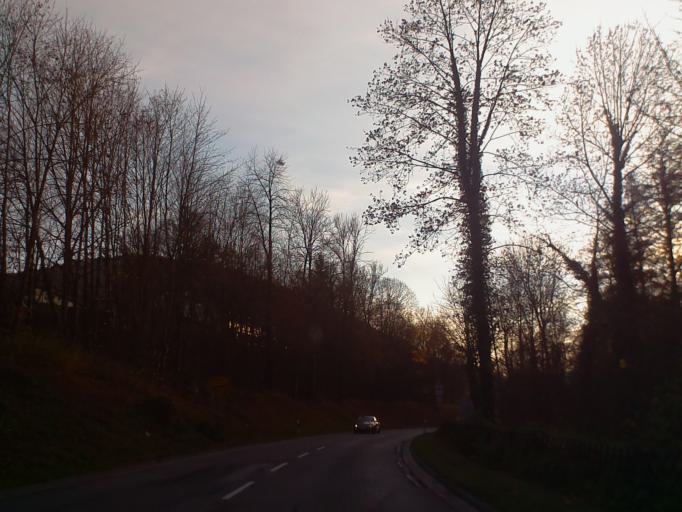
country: DE
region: Bavaria
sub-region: Regierungsbezirk Unterfranken
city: Weilbach
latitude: 49.6410
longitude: 9.2196
